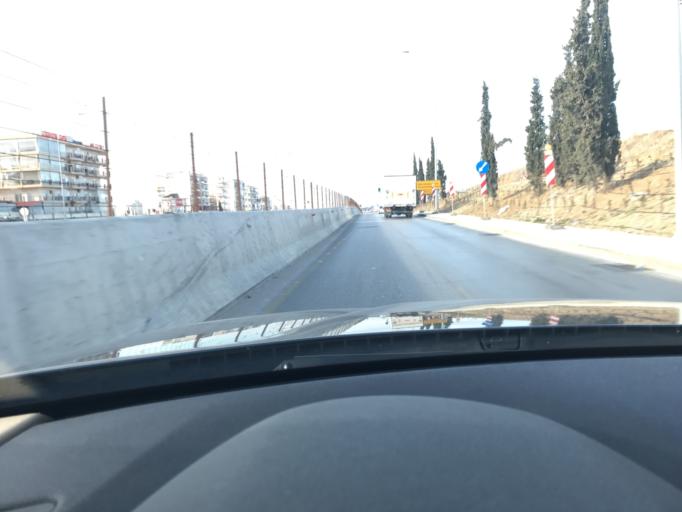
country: GR
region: Central Macedonia
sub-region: Nomos Thessalonikis
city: Evosmos
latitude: 40.6779
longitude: 22.9084
